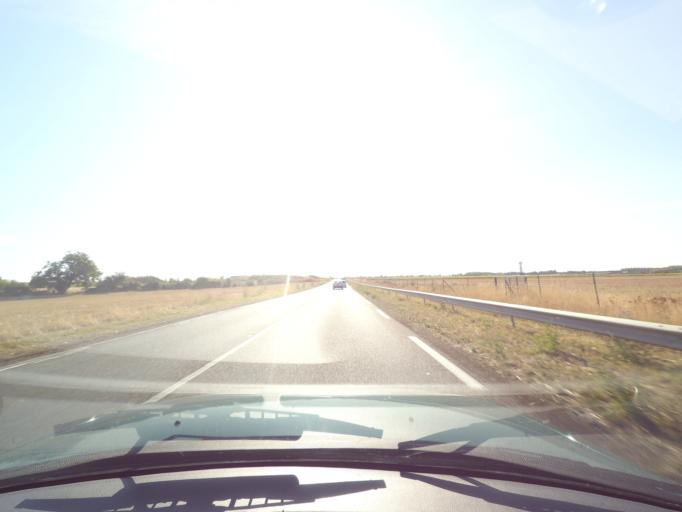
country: FR
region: Poitou-Charentes
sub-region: Departement de la Vienne
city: Vouille
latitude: 46.6493
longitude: 0.1498
